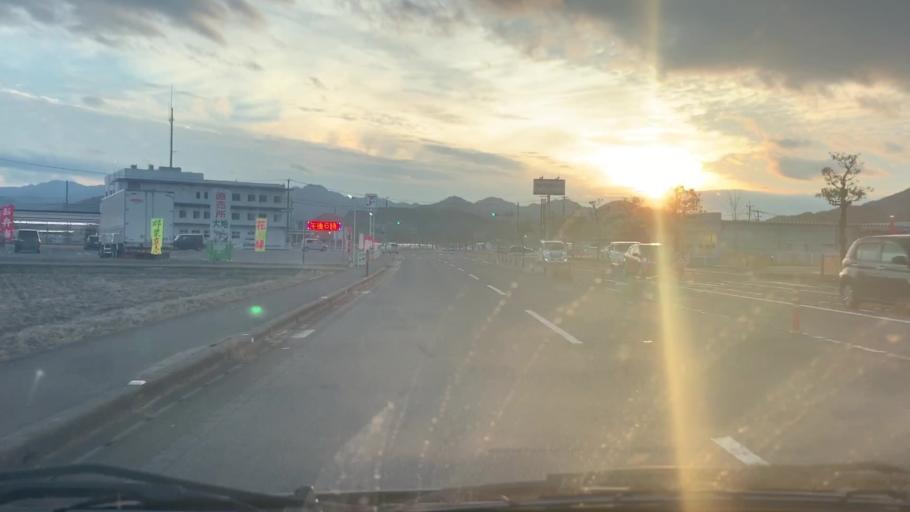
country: JP
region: Saga Prefecture
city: Kashima
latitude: 33.1200
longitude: 130.0921
